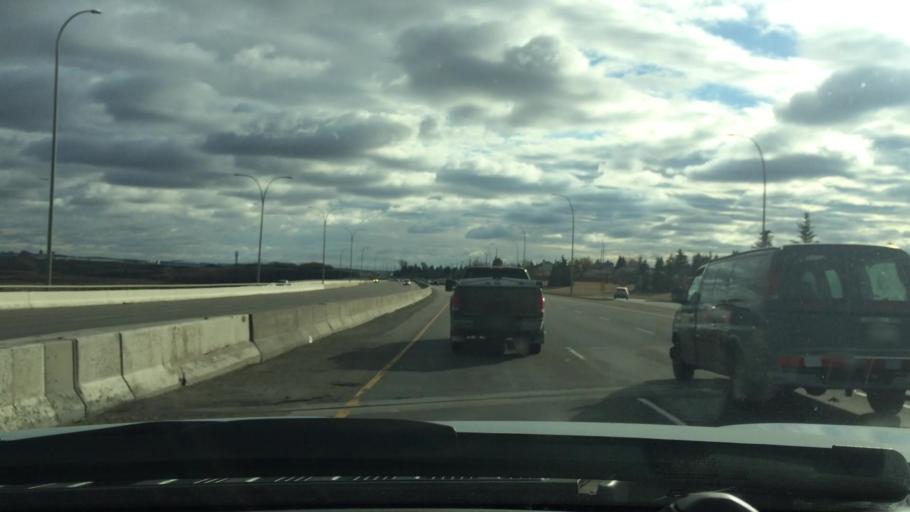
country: CA
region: Alberta
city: Calgary
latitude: 51.1343
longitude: -114.0713
